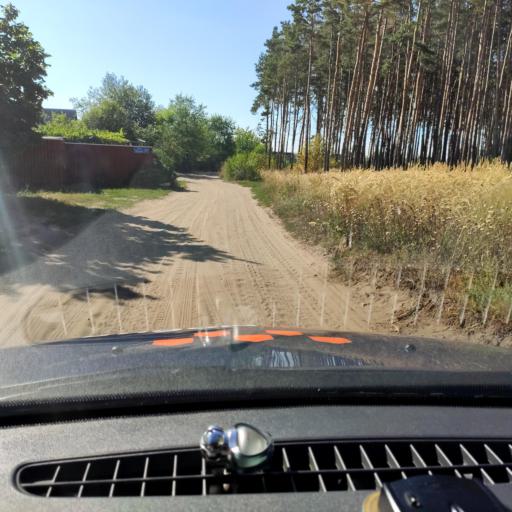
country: RU
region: Voronezj
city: Shilovo
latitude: 51.5328
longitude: 39.1599
